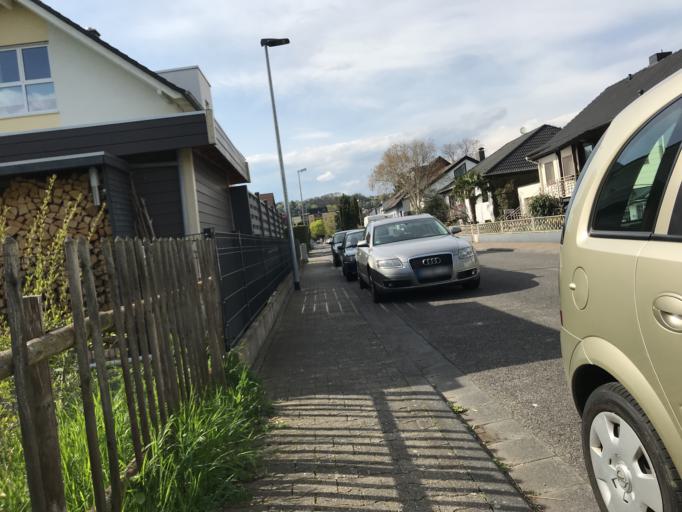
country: DE
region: Rheinland-Pfalz
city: Bodenheim
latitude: 49.9596
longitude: 8.3195
